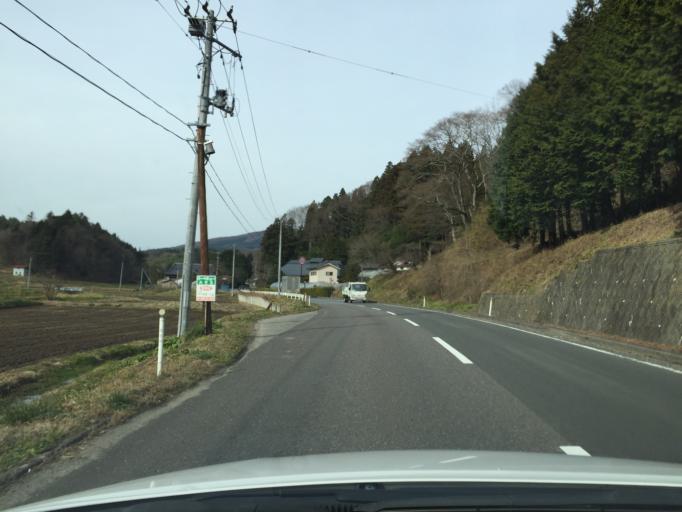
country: JP
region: Fukushima
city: Funehikimachi-funehiki
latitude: 37.3262
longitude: 140.6141
